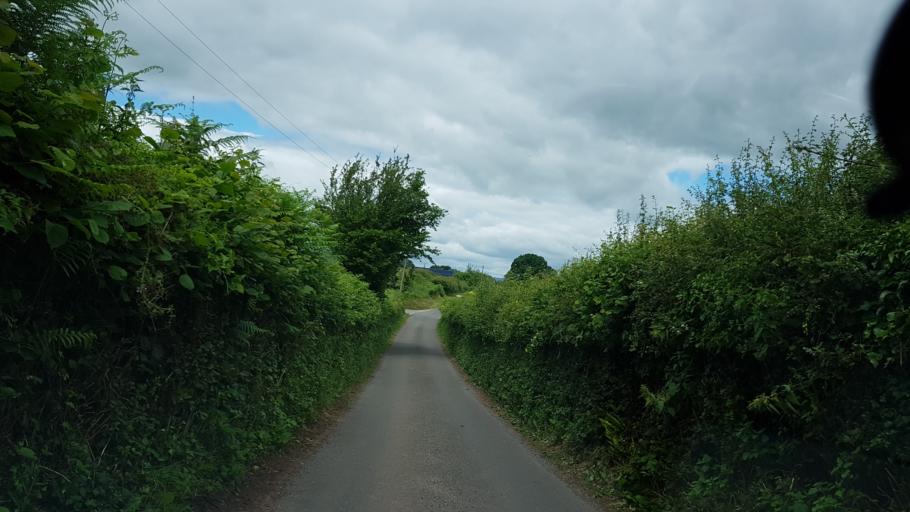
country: GB
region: Wales
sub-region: Monmouthshire
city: Llanarth
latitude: 51.8066
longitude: -2.8418
